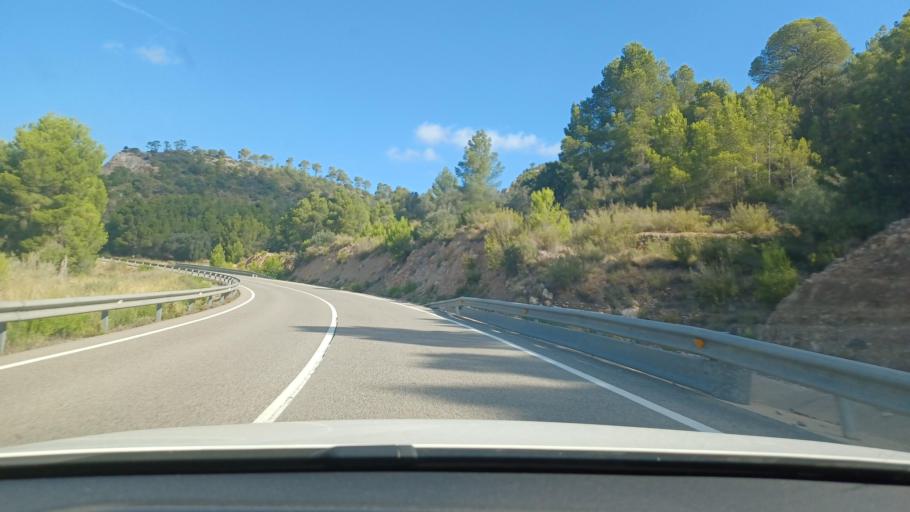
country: ES
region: Catalonia
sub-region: Provincia de Tarragona
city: Benifallet
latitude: 40.9635
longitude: 0.4480
